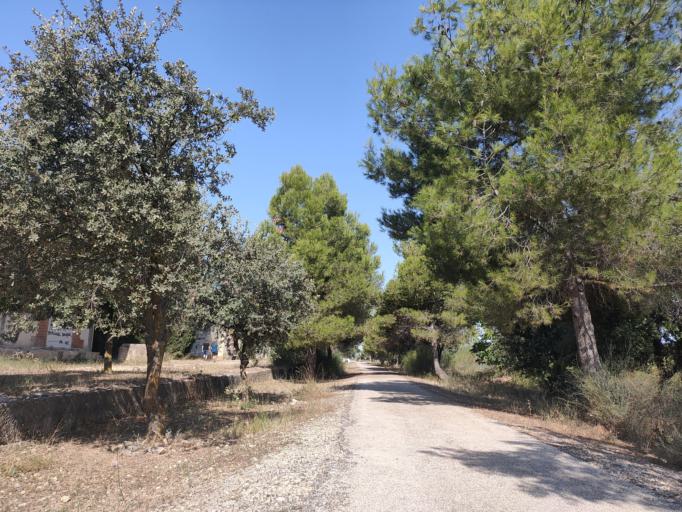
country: ES
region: Catalonia
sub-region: Provincia de Tarragona
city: Horta de Sant Joan
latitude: 40.9644
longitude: 0.3207
